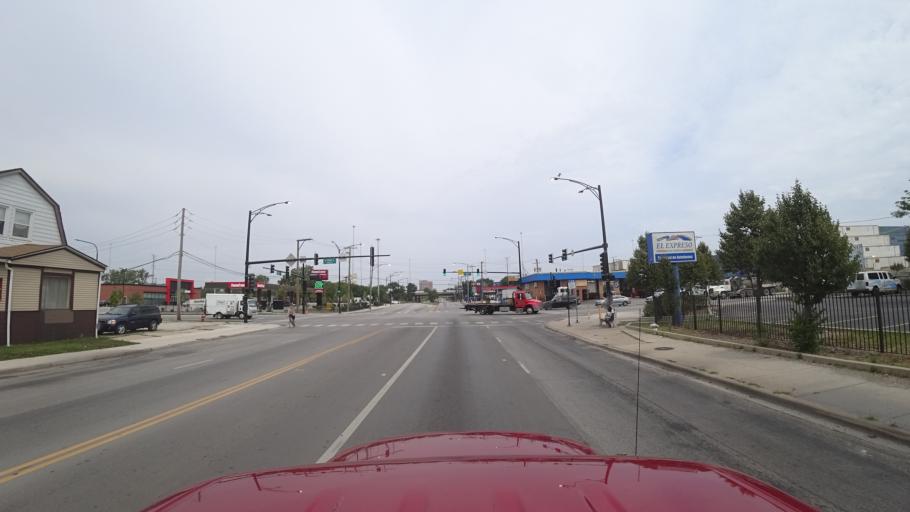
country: US
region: Illinois
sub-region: Cook County
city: Chicago
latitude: 41.8297
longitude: -87.6948
